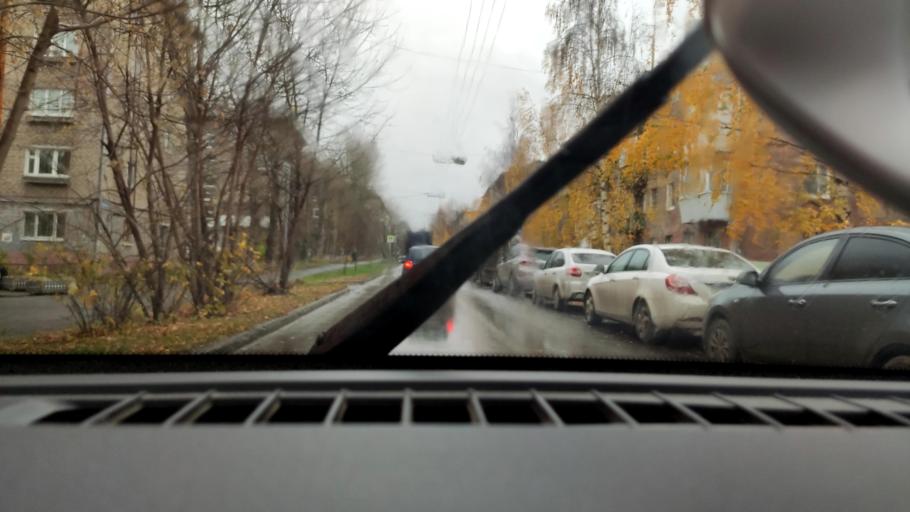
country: RU
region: Perm
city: Kondratovo
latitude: 57.9771
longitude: 56.1708
